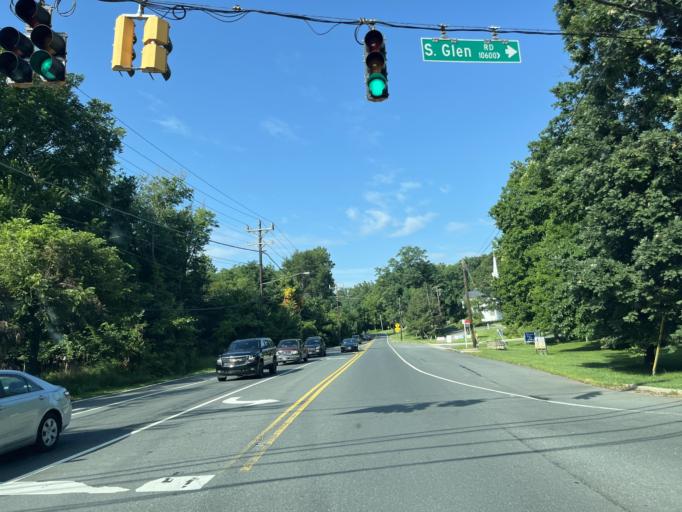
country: US
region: Maryland
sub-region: Montgomery County
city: Potomac
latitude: 39.0266
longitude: -77.2040
